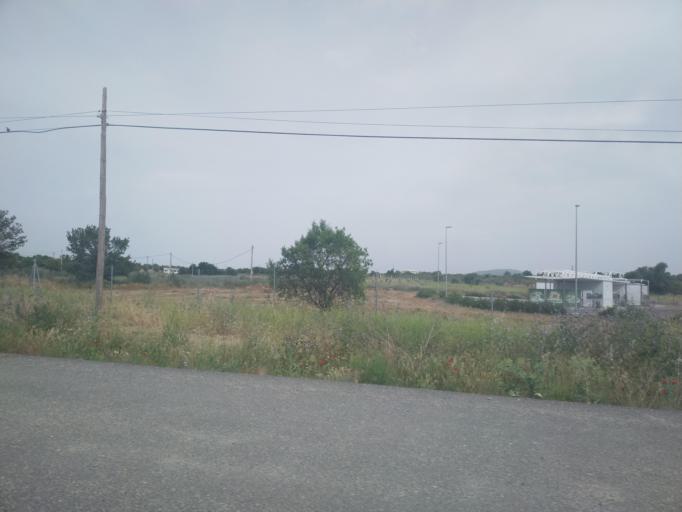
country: ES
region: Castille-La Mancha
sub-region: Province of Toledo
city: Guadamur
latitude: 39.8036
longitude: -4.1336
